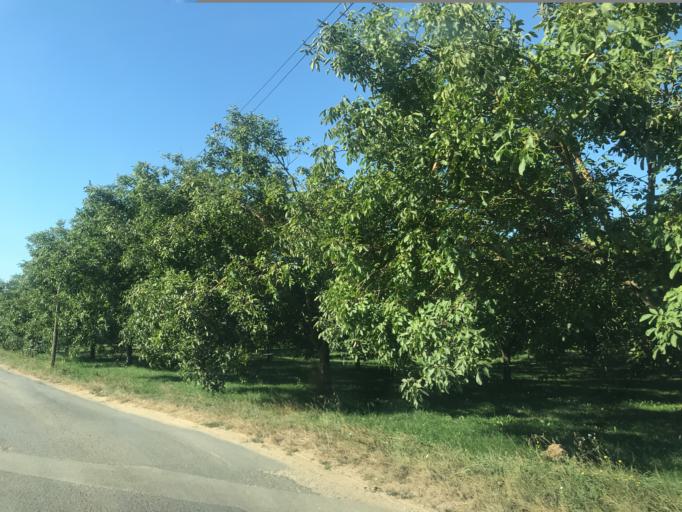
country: FR
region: Aquitaine
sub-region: Departement de la Dordogne
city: Cenac-et-Saint-Julien
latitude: 44.8169
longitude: 1.1854
